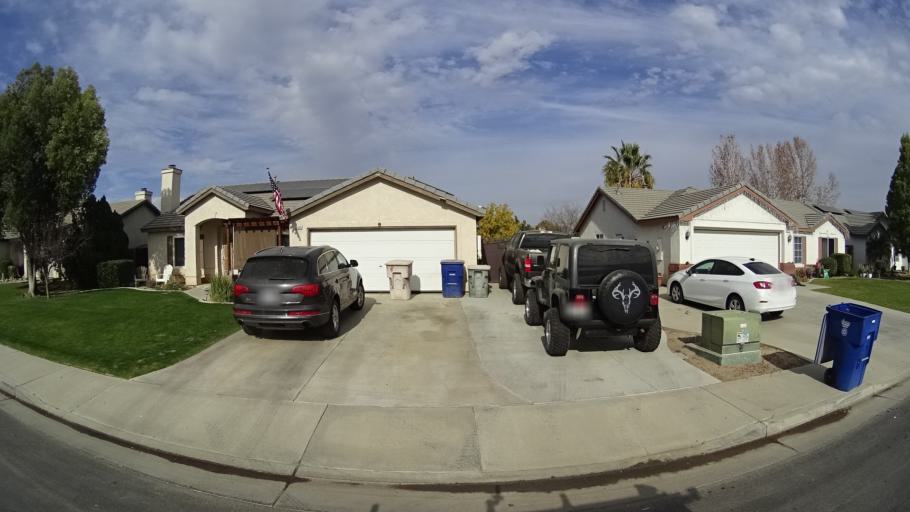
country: US
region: California
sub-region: Kern County
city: Greenacres
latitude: 35.4119
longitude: -119.1222
